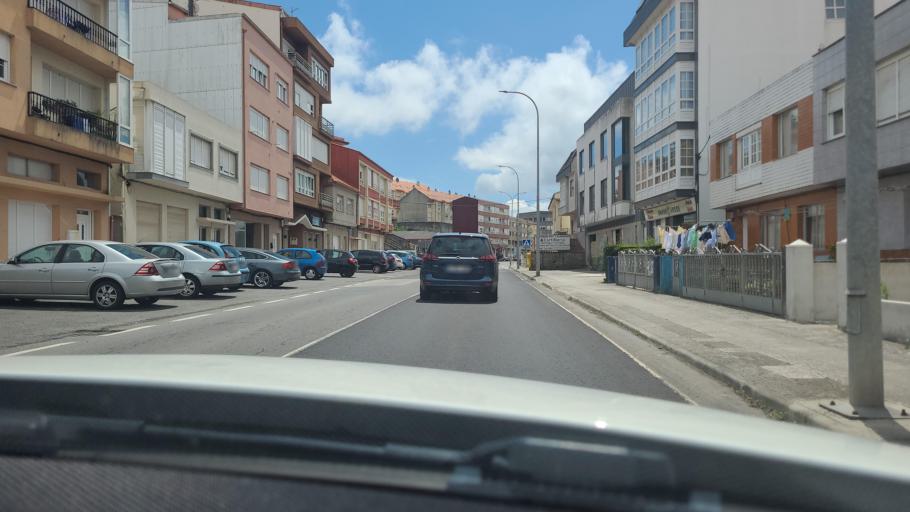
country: ES
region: Galicia
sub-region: Provincia da Coruna
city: Cee
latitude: 42.9530
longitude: -9.1862
